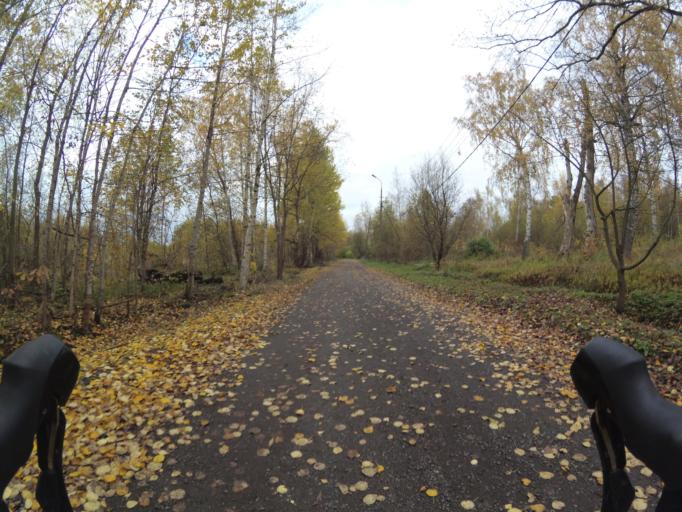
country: RU
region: St.-Petersburg
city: Lakhtinskiy
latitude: 59.9960
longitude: 30.1631
